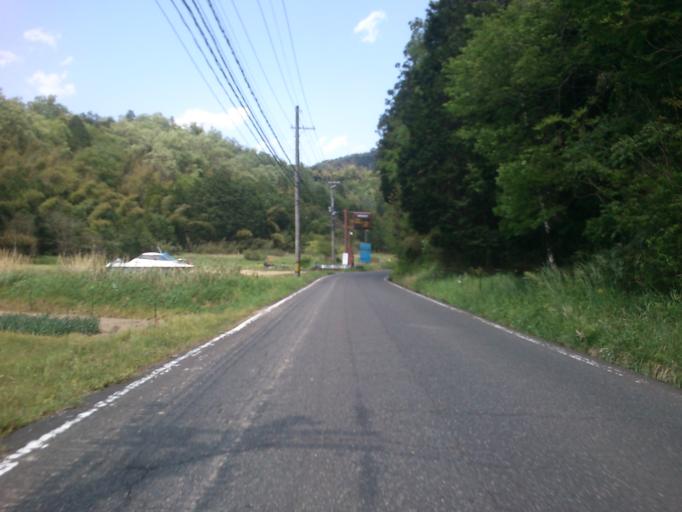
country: JP
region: Kyoto
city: Miyazu
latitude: 35.6840
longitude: 135.1111
